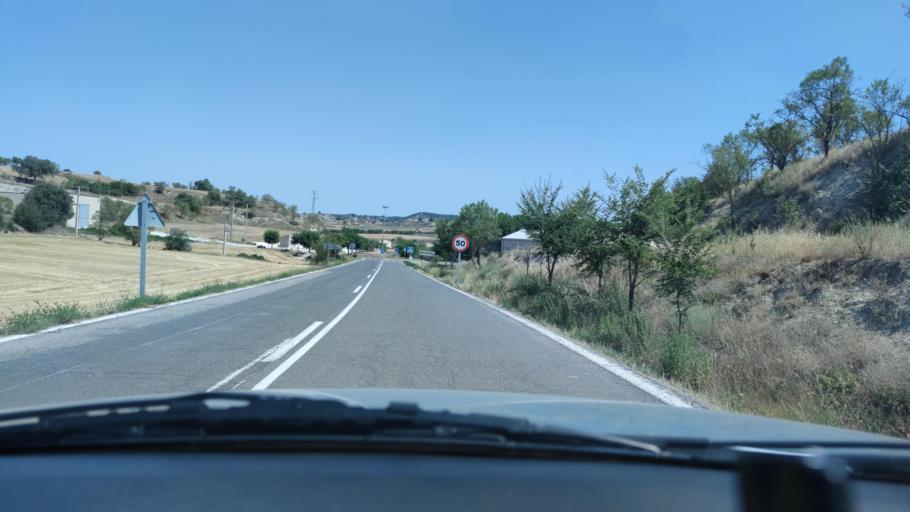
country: ES
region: Catalonia
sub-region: Provincia de Lleida
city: Cervera
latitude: 41.6243
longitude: 1.3398
